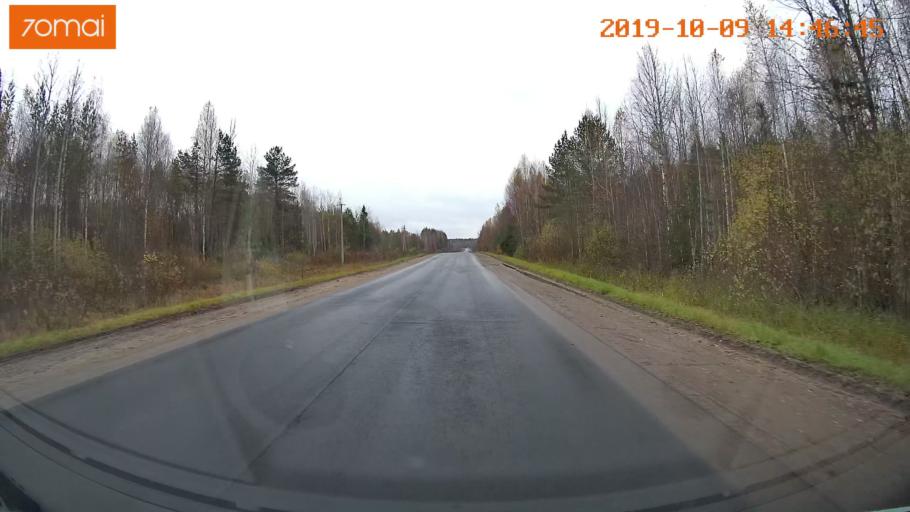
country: RU
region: Kostroma
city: Buy
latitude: 58.4270
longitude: 41.5756
